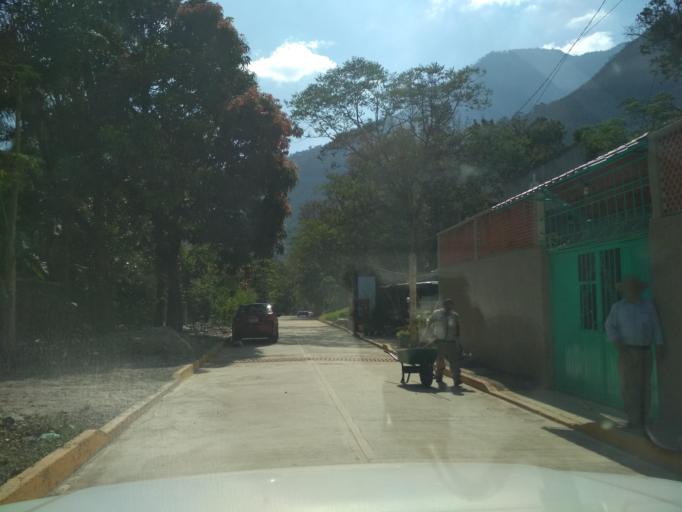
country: MX
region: Veracruz
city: Jalapilla
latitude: 18.8057
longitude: -97.1019
